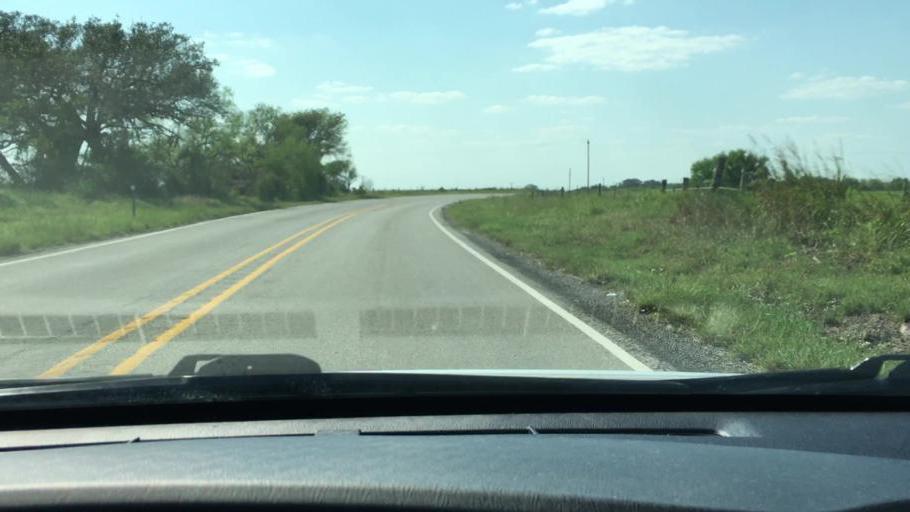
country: US
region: Texas
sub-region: DeWitt County
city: Yorktown
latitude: 28.9233
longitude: -97.3524
